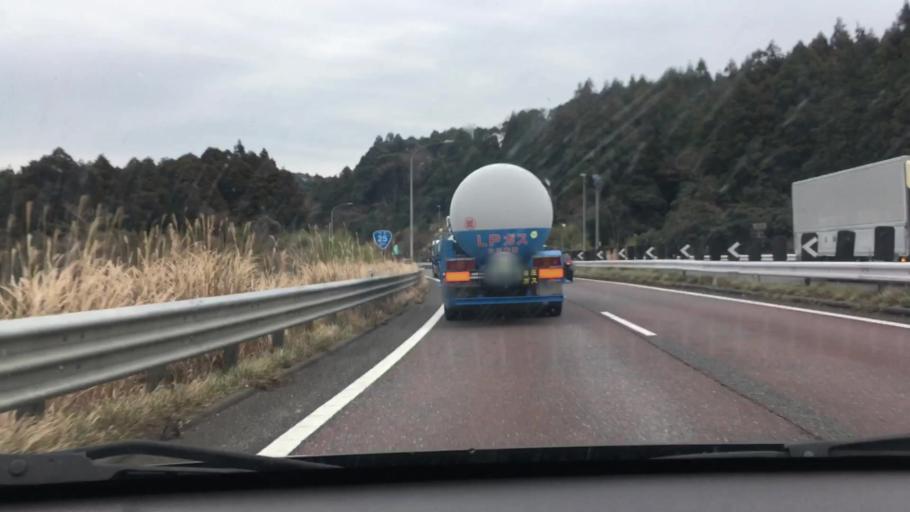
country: JP
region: Mie
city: Kameyama
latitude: 34.8385
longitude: 136.3778
